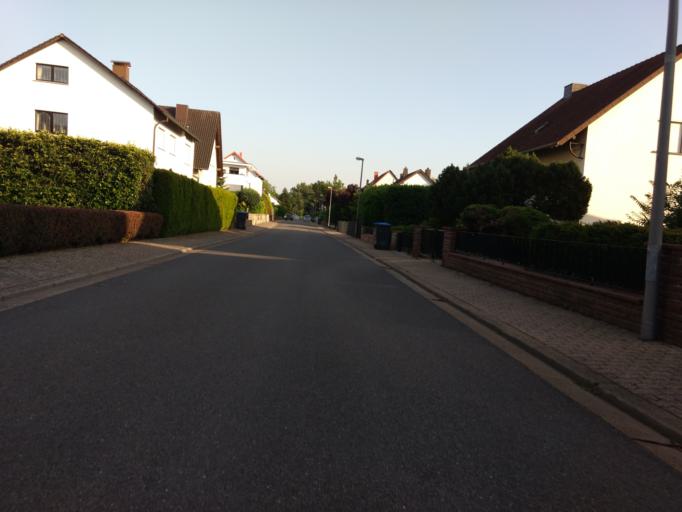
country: DE
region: Saarland
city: Saarlouis
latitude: 49.3063
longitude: 6.7480
